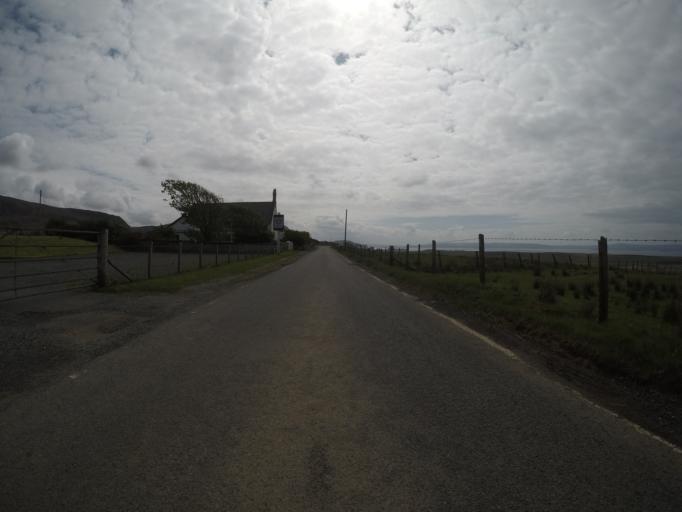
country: GB
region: Scotland
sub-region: Highland
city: Portree
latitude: 57.6369
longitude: -6.3764
